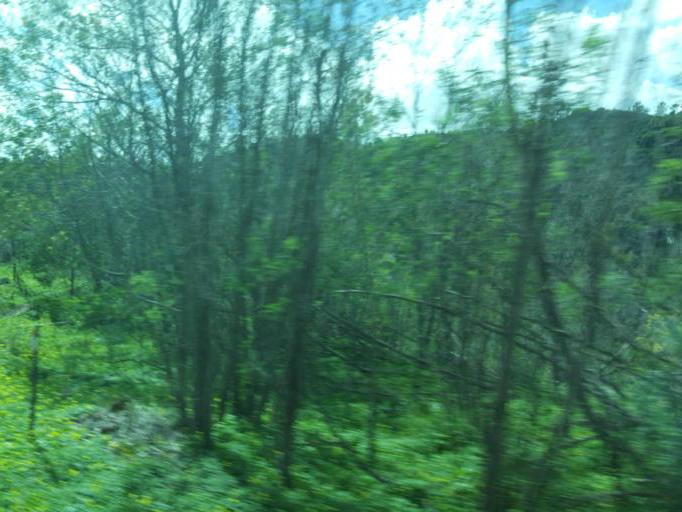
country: PT
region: Faro
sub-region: Monchique
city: Monchique
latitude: 37.2755
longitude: -8.5502
